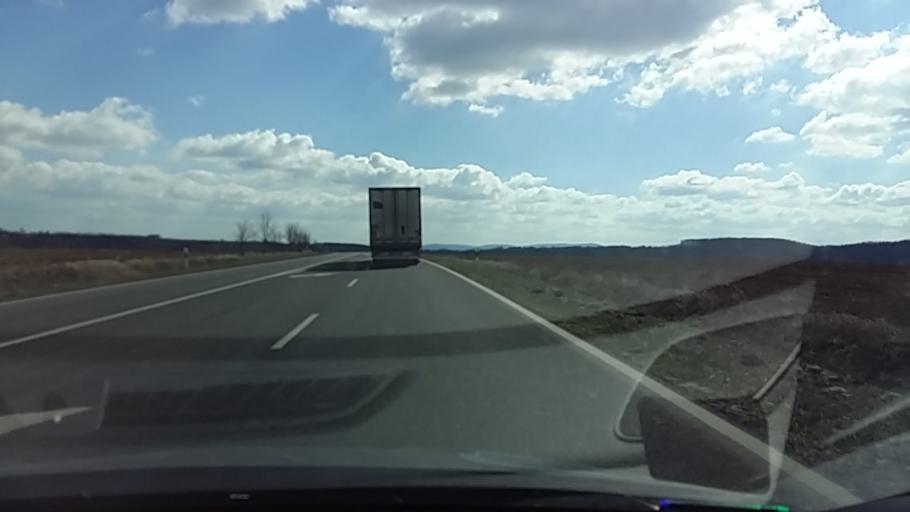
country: HU
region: Baranya
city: Kozarmisleny
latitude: 46.0349
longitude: 18.2730
